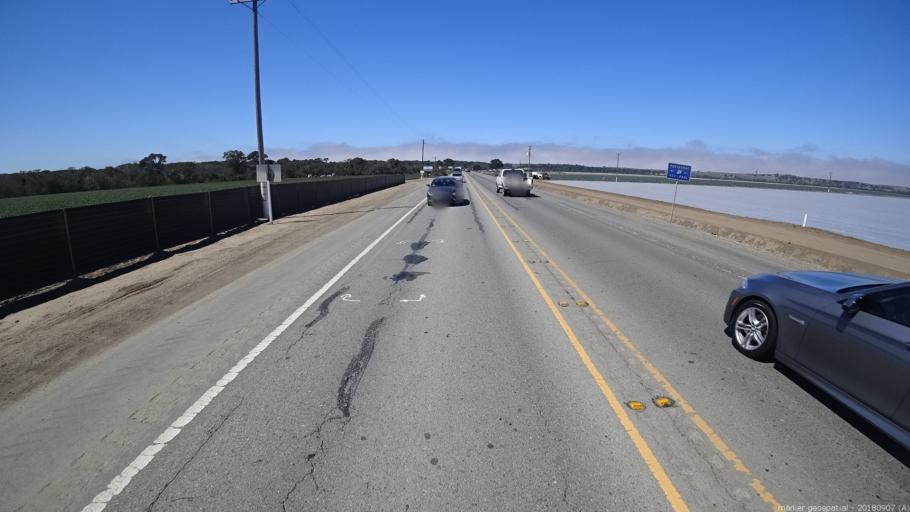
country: US
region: California
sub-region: Monterey County
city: Marina
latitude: 36.6786
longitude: -121.7384
